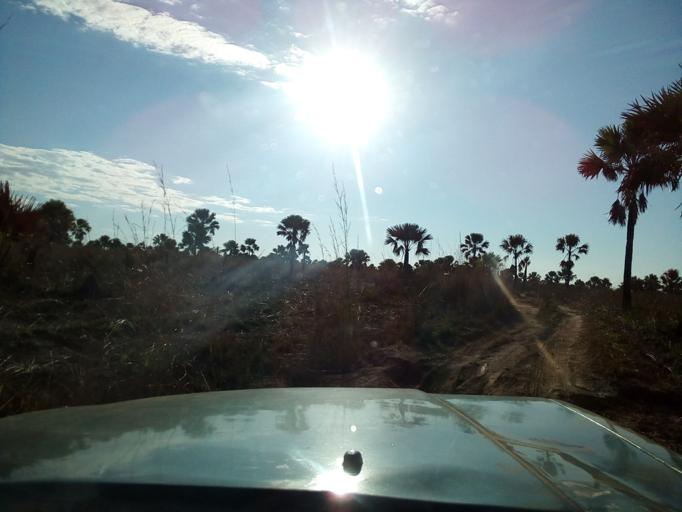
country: MG
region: Boeny
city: Sitampiky
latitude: -16.1328
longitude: 45.5488
